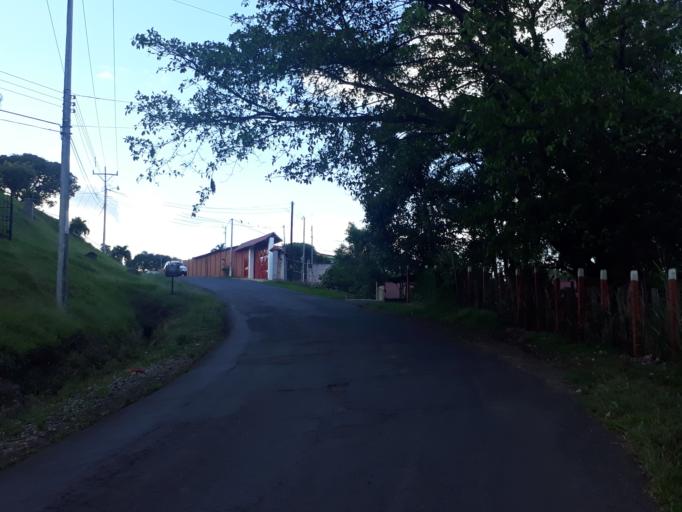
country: CR
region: Alajuela
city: Carrillos
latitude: 10.0390
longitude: -84.3277
